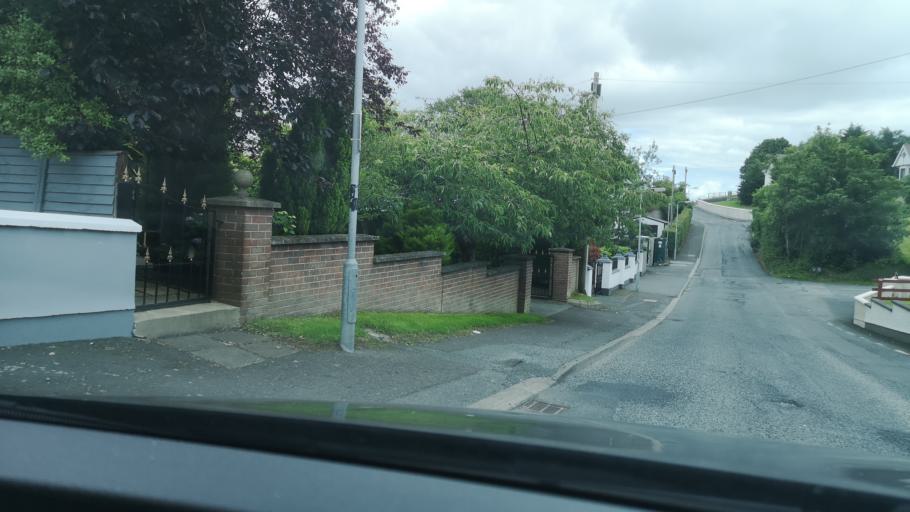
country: GB
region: Northern Ireland
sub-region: Newry and Mourne District
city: Newry
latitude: 54.1712
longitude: -6.3285
